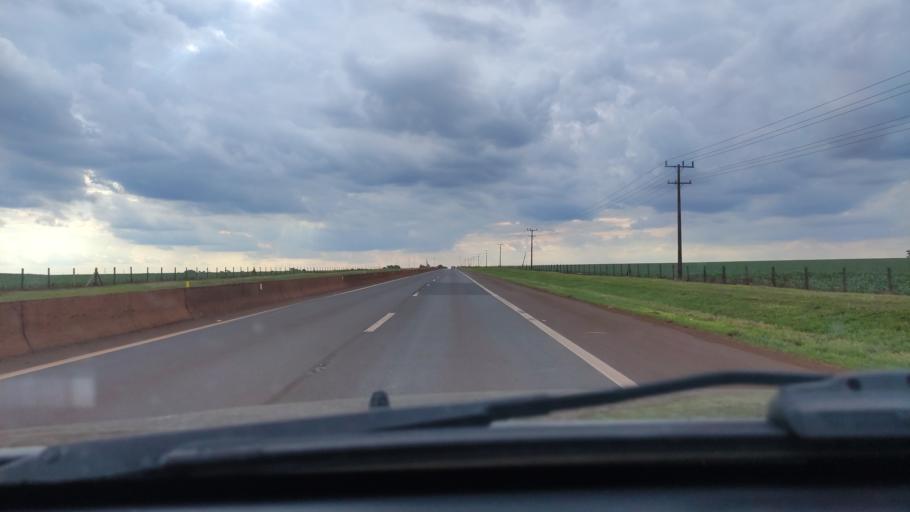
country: BR
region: Sao Paulo
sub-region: Palmital
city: Palmital
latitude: -22.8220
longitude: -50.0412
